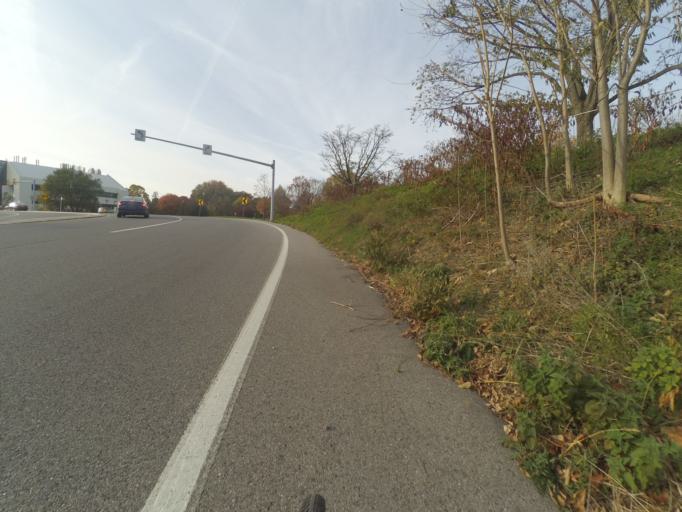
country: US
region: Pennsylvania
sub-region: Centre County
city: State College
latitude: 40.8034
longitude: -77.8505
